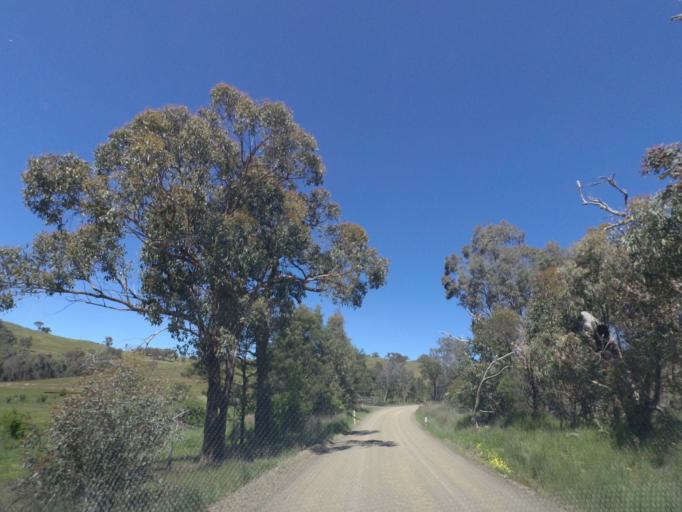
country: AU
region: Victoria
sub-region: Whittlesea
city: Whittlesea
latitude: -37.2785
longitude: 145.0153
